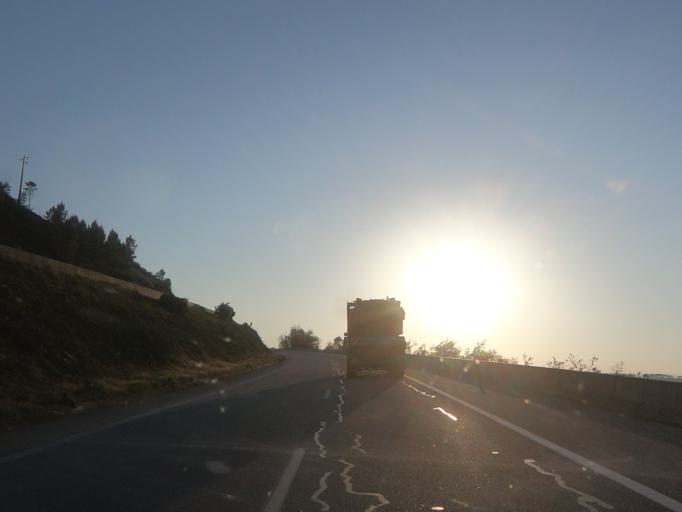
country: PT
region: Viseu
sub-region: Mangualde
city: Mangualde
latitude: 40.6179
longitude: -7.7337
